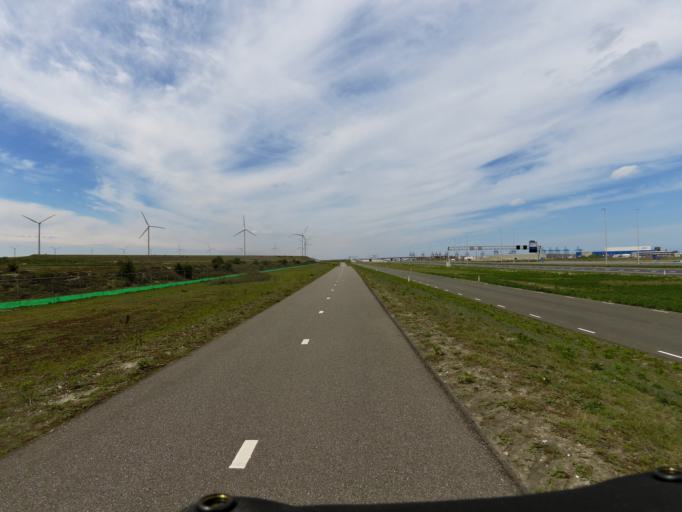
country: NL
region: South Holland
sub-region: Gemeente Rotterdam
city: Hoek van Holland
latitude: 51.9291
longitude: 4.0293
